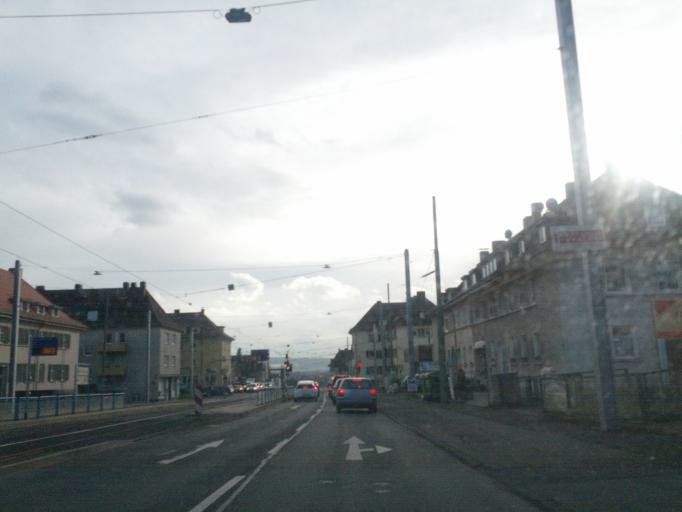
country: DE
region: Hesse
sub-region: Regierungsbezirk Kassel
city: Kassel
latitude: 51.3316
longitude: 9.5133
